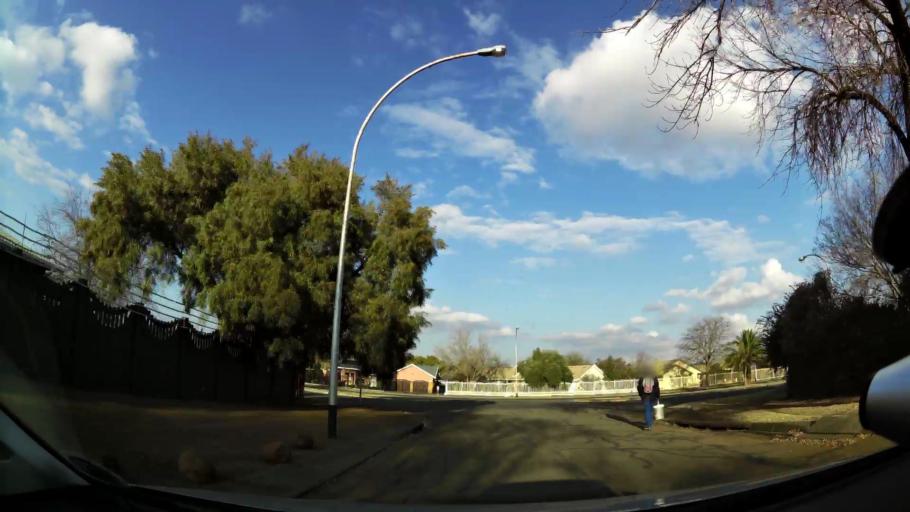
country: ZA
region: Orange Free State
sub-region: Mangaung Metropolitan Municipality
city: Bloemfontein
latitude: -29.1517
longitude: 26.1847
